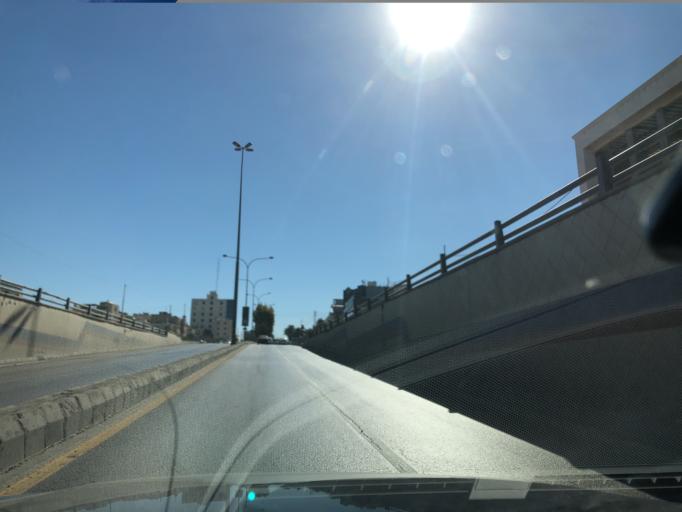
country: JO
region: Amman
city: Al Jubayhah
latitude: 31.9743
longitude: 35.8665
